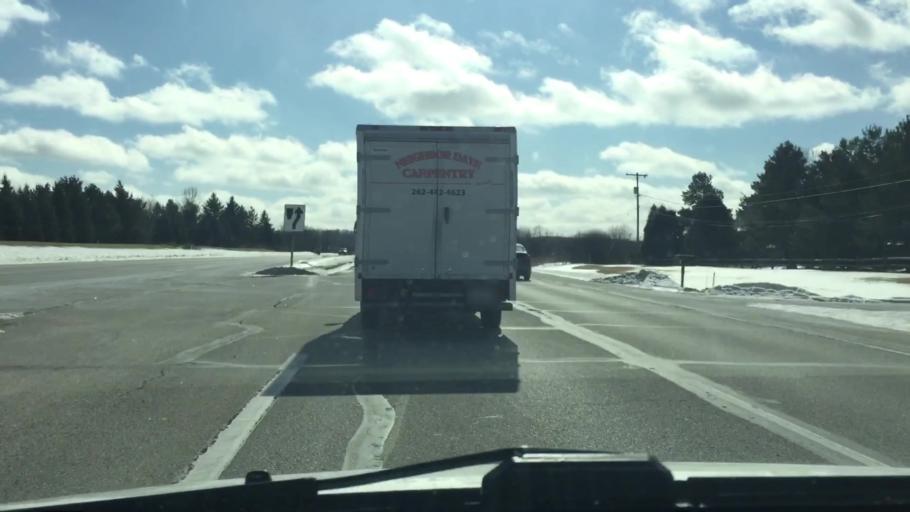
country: US
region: Wisconsin
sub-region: Waukesha County
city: Waukesha
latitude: 42.9541
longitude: -88.2282
